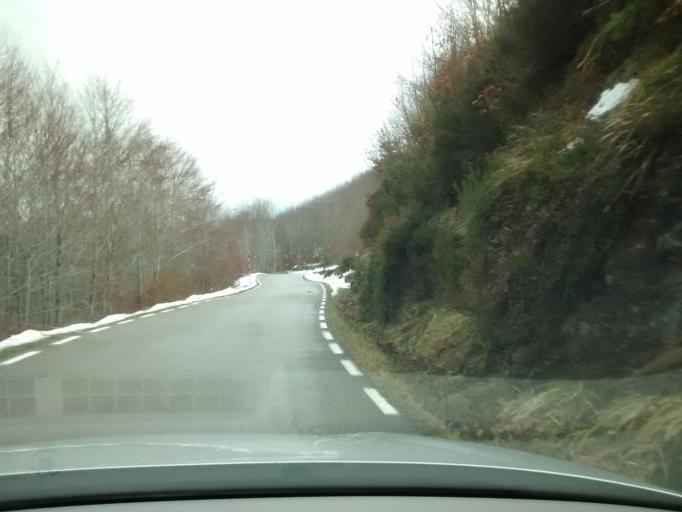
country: ES
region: Castille and Leon
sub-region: Provincia de Burgos
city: Espinosa de los Monteros
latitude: 43.1244
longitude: -3.6295
